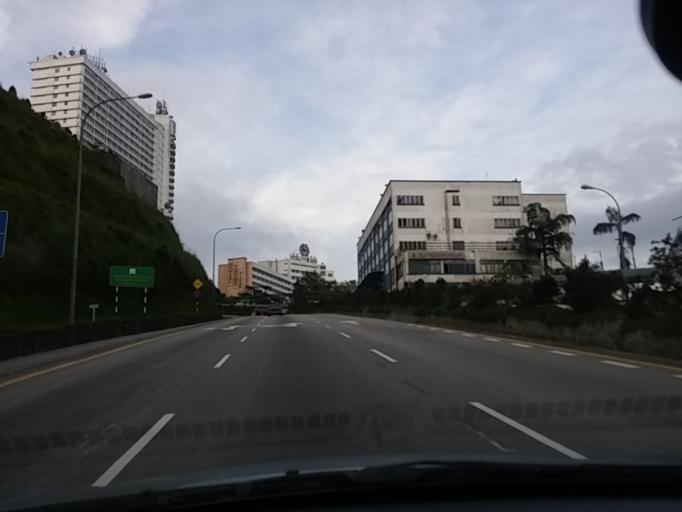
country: MY
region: Pahang
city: Kampung Bukit Tinggi, Bentong
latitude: 3.4206
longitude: 101.7909
